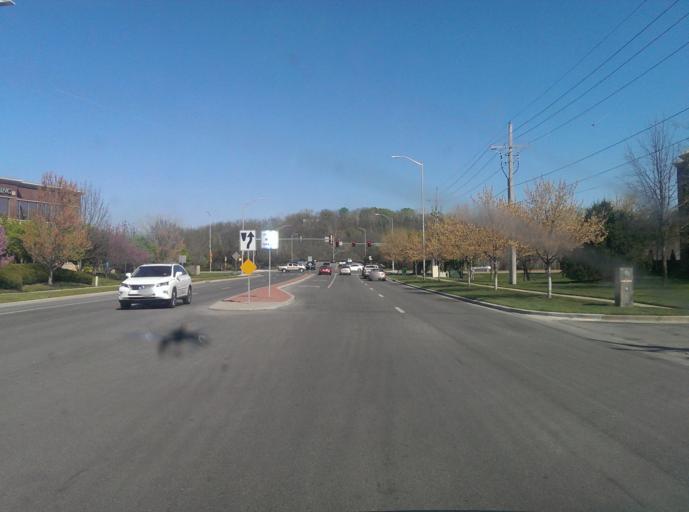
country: US
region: Kansas
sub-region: Johnson County
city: Leawood
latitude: 38.9275
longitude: -94.6267
